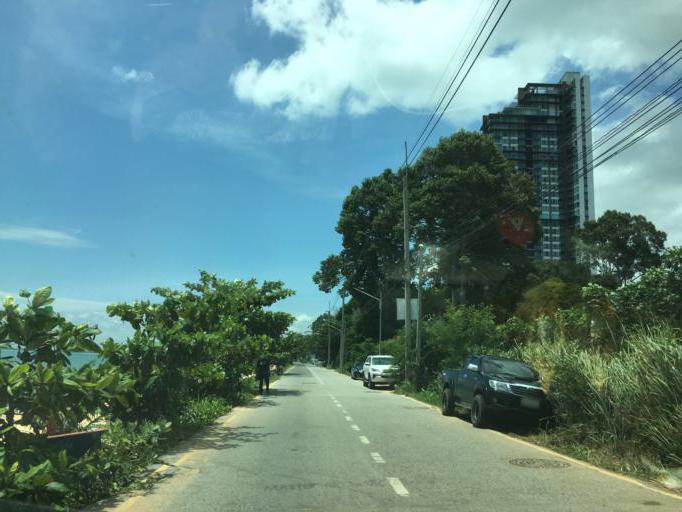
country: TH
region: Chon Buri
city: Sattahip
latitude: 12.7720
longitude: 100.8995
